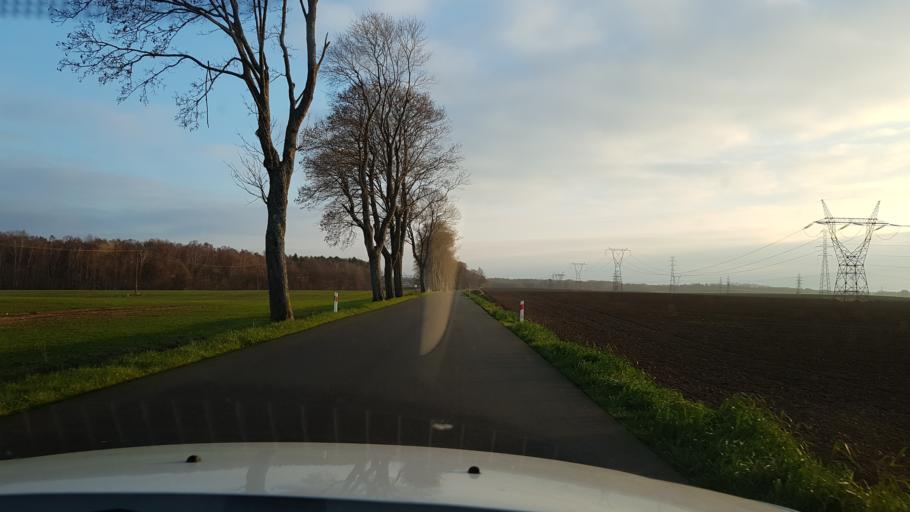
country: PL
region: West Pomeranian Voivodeship
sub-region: Koszalin
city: Koszalin
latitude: 54.1358
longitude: 16.0834
